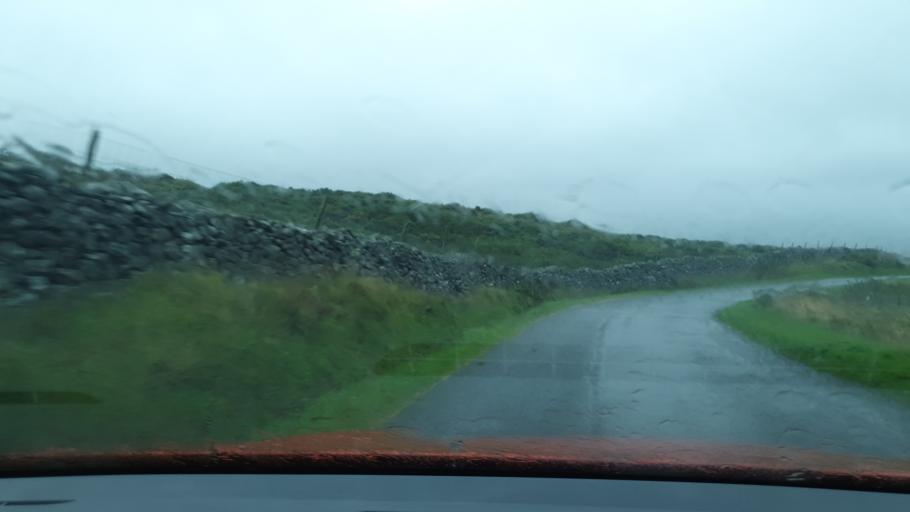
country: GB
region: England
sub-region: Cumbria
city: Millom
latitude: 54.3491
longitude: -3.2527
